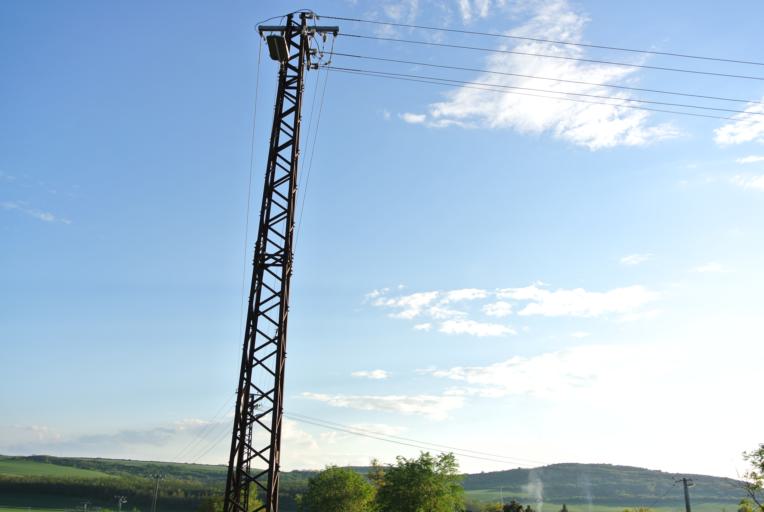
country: HU
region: Komarom-Esztergom
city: Sarisap
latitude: 47.6646
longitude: 18.6949
